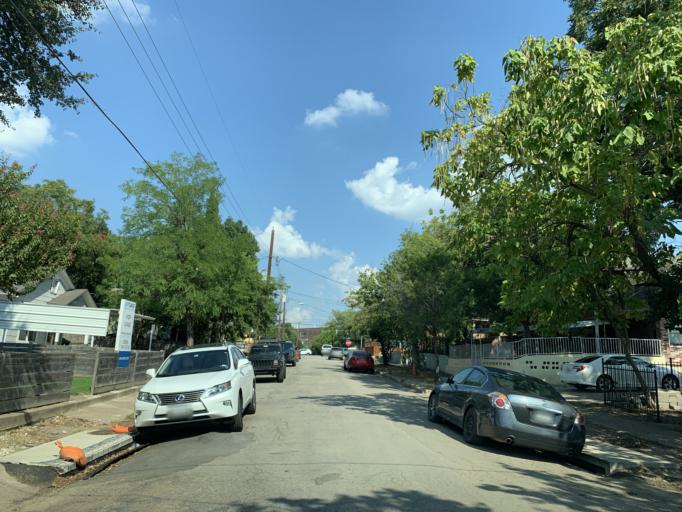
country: US
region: Texas
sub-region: Dallas County
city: Dallas
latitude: 32.7481
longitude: -96.8258
